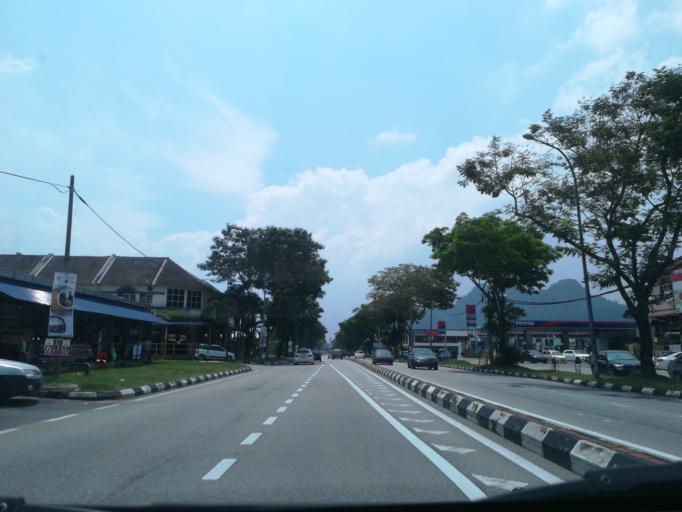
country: MY
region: Perak
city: Ipoh
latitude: 4.5789
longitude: 101.1273
